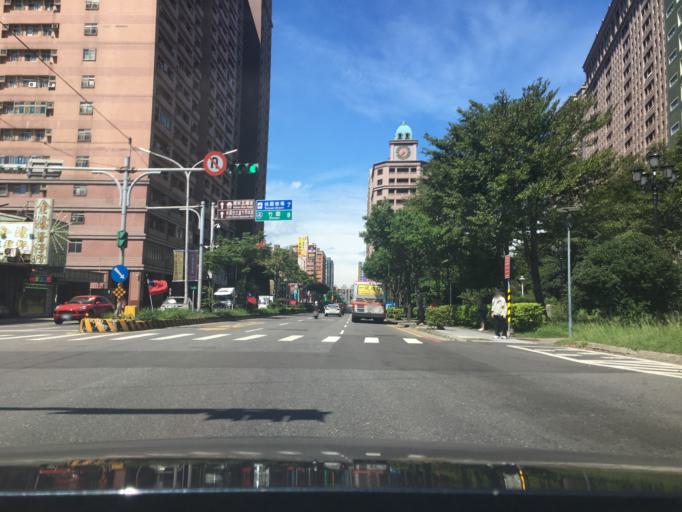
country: TW
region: Taiwan
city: Taoyuan City
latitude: 25.0416
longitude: 121.2955
